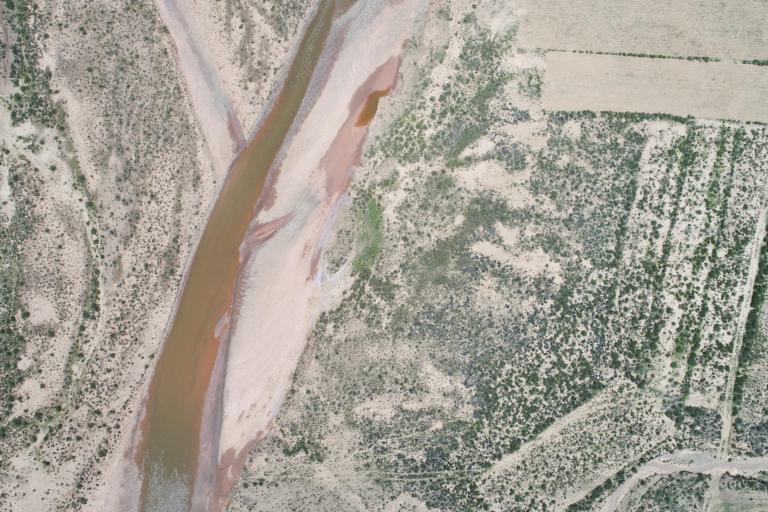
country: BO
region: La Paz
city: Curahuara de Carangas
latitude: -17.3200
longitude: -68.5135
